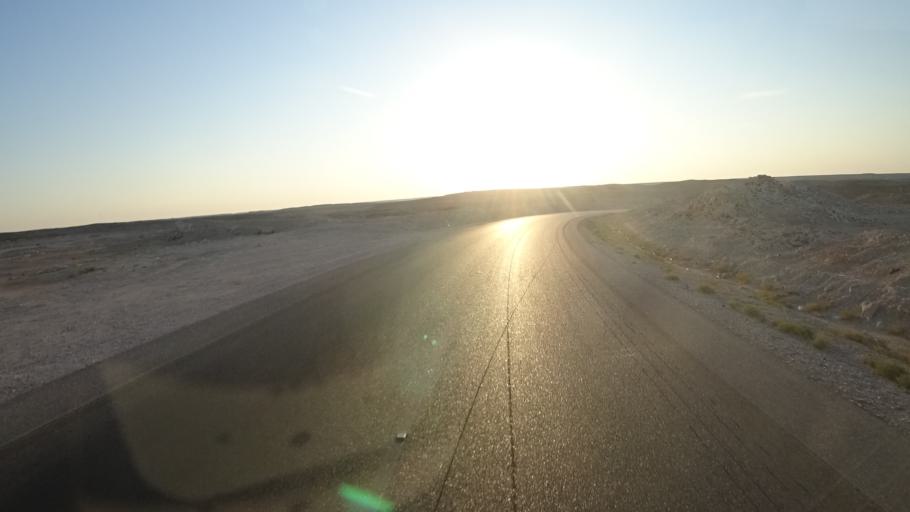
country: OM
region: Zufar
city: Salalah
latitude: 17.5268
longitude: 53.3971
